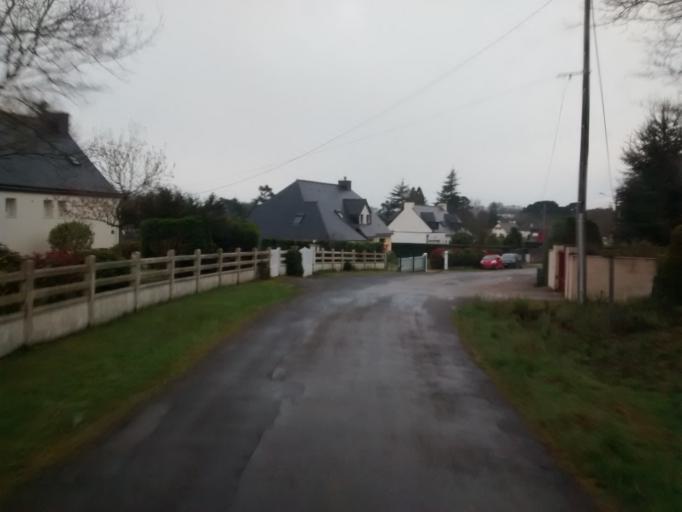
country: FR
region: Brittany
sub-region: Departement du Morbihan
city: Malestroit
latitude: 47.8102
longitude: -2.3997
